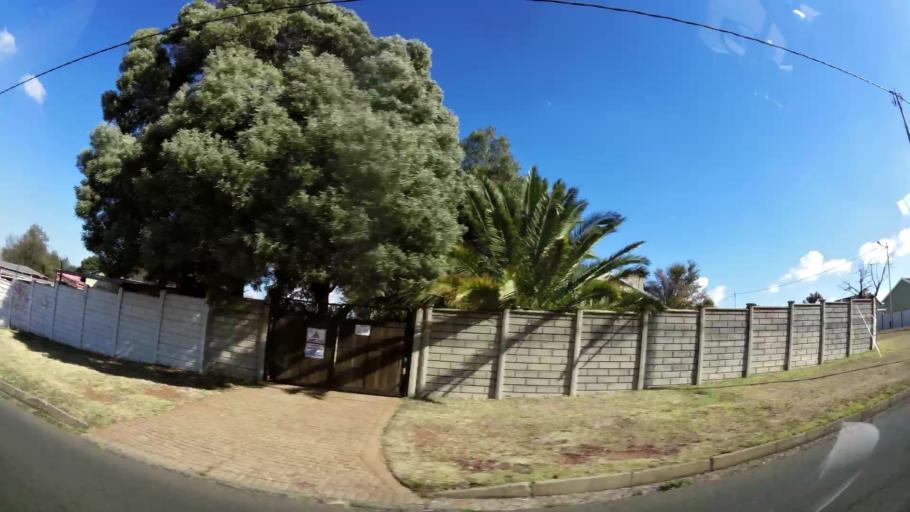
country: ZA
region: Gauteng
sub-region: City of Johannesburg Metropolitan Municipality
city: Roodepoort
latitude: -26.1471
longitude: 27.8339
